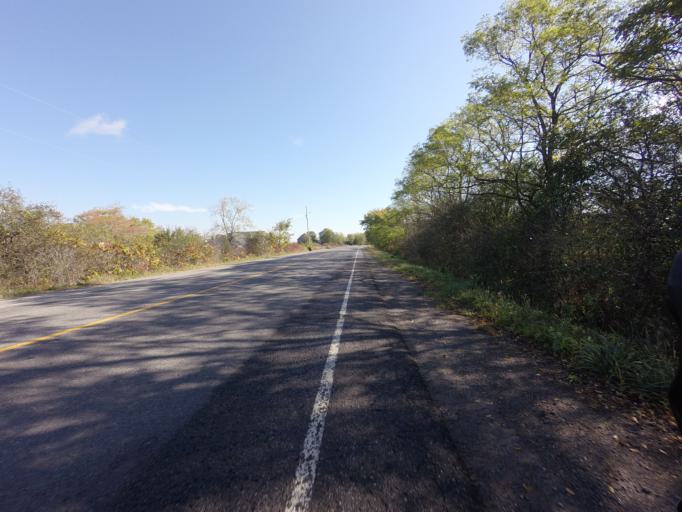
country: CA
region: Ontario
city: Prince Edward
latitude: 44.0155
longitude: -77.3231
